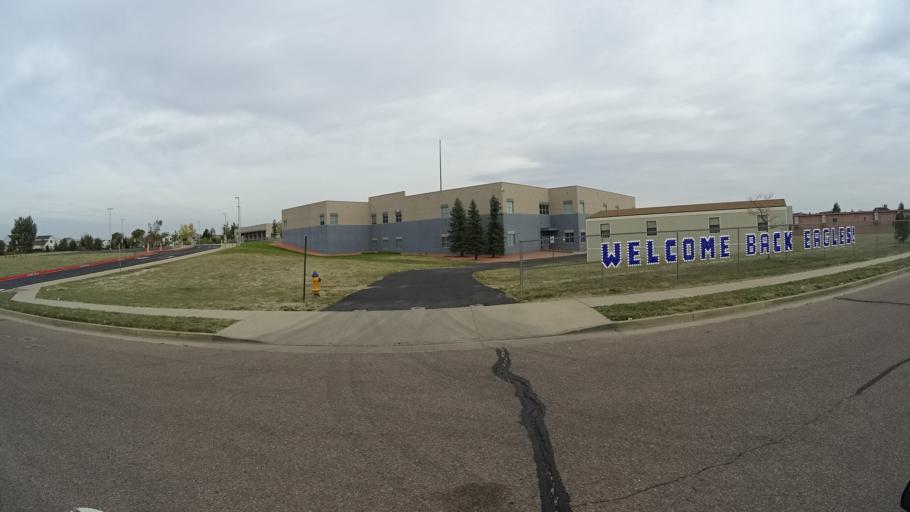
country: US
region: Colorado
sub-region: El Paso County
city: Cimarron Hills
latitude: 38.9191
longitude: -104.7096
